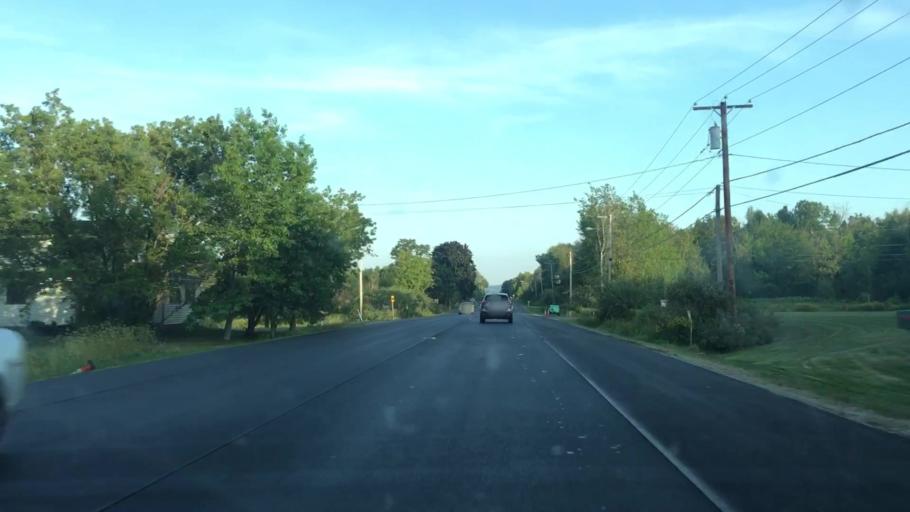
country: US
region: Maine
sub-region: Penobscot County
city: Hampden
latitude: 44.7613
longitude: -68.8483
